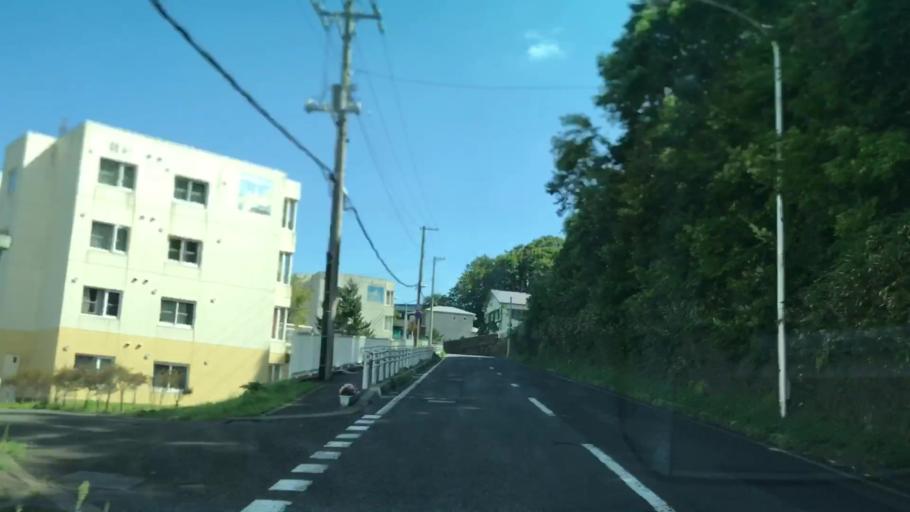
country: JP
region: Hokkaido
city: Muroran
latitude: 42.3064
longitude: 141.0015
